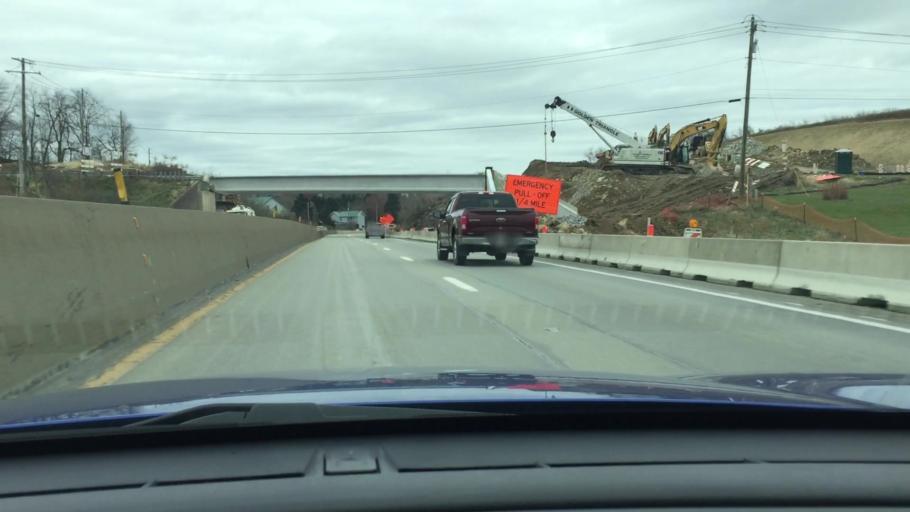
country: US
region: Pennsylvania
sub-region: Westmoreland County
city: West Newton
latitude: 40.1824
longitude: -79.7104
